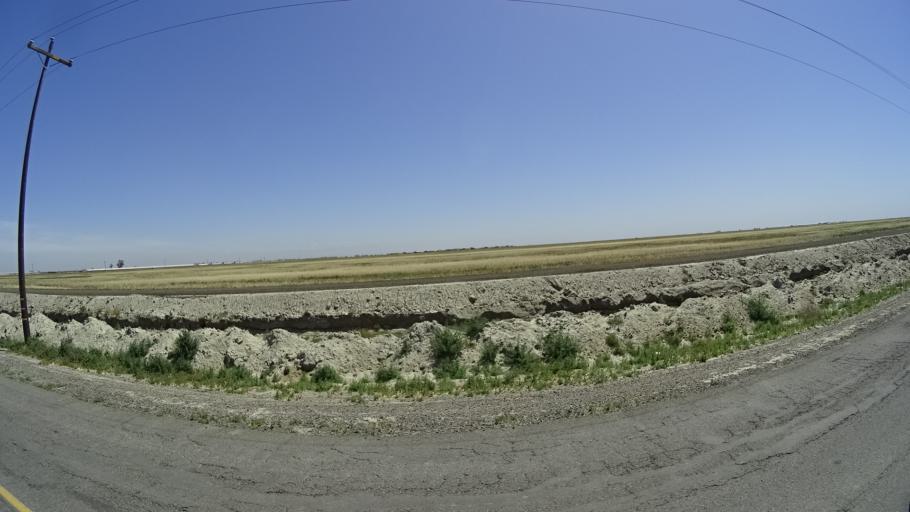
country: US
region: California
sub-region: Kings County
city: Stratford
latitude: 36.1864
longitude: -119.7175
